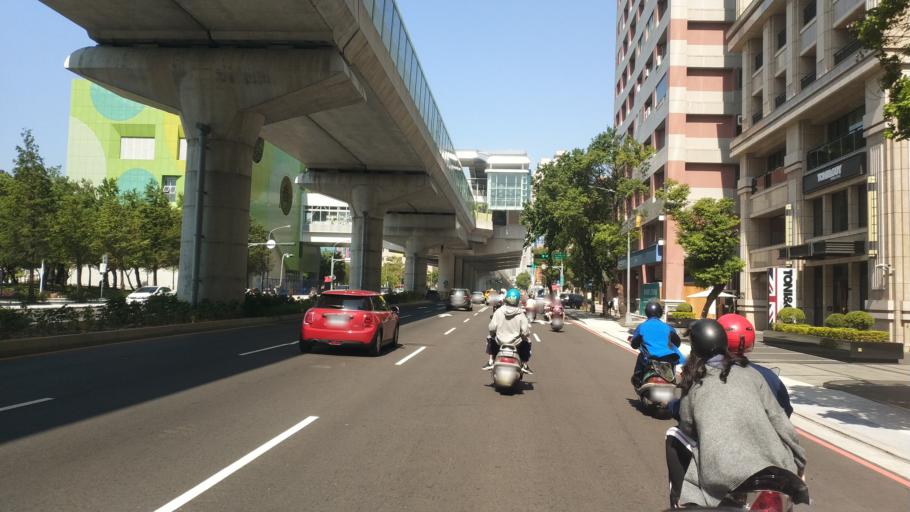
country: TW
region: Taiwan
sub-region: Taichung City
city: Taichung
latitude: 24.1441
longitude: 120.6468
